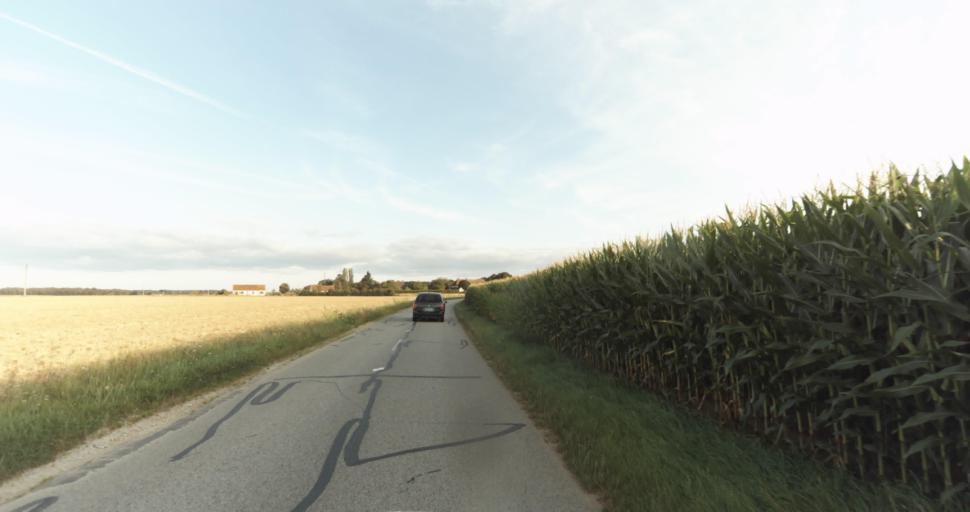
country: FR
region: Haute-Normandie
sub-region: Departement de l'Eure
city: Saint-Germain-sur-Avre
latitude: 48.8462
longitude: 1.2522
